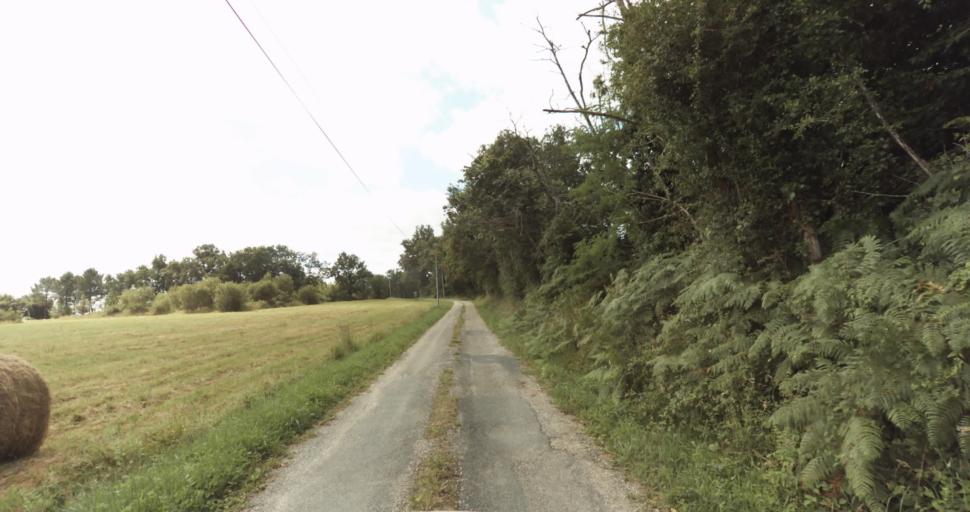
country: FR
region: Aquitaine
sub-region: Departement de la Gironde
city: Bazas
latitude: 44.4678
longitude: -0.1749
